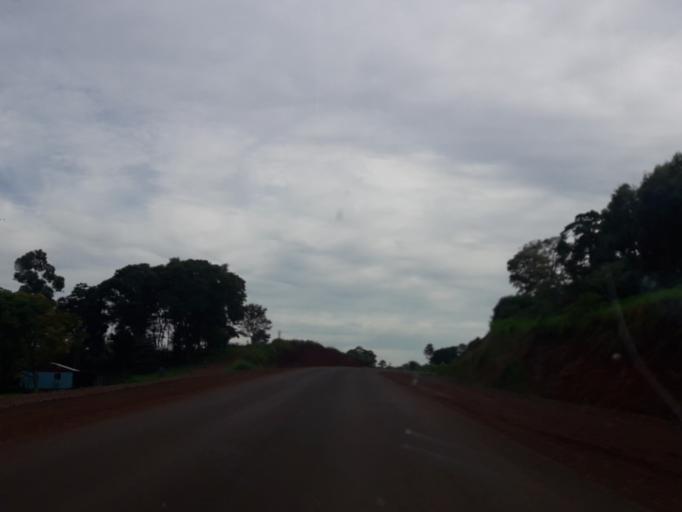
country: AR
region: Misiones
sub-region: Departamento de San Pedro
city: San Pedro
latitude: -26.5107
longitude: -53.9236
